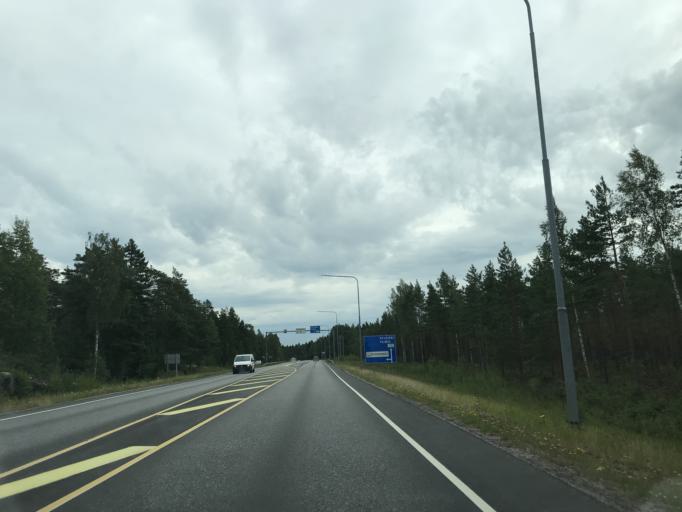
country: FI
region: Varsinais-Suomi
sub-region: Turku
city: Paimio
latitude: 60.4223
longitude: 22.7138
